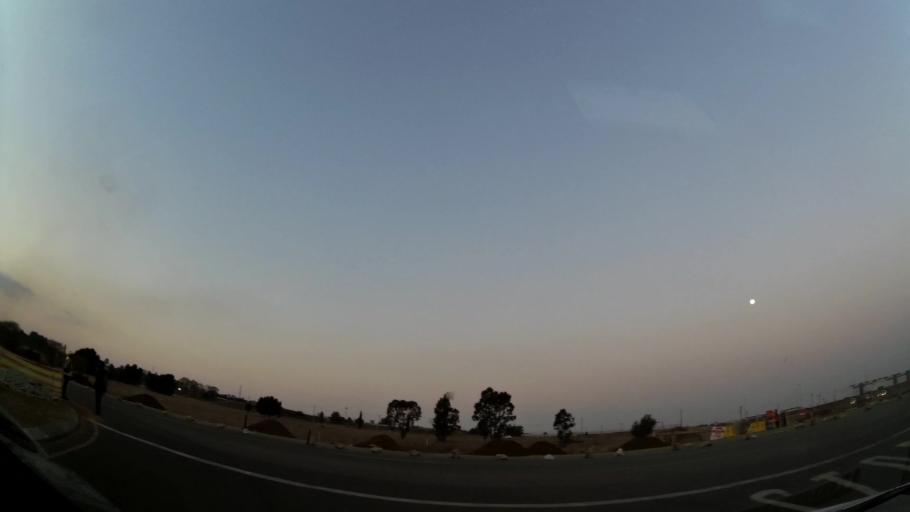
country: ZA
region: Gauteng
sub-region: Ekurhuleni Metropolitan Municipality
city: Nigel
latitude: -26.3525
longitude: 28.4548
